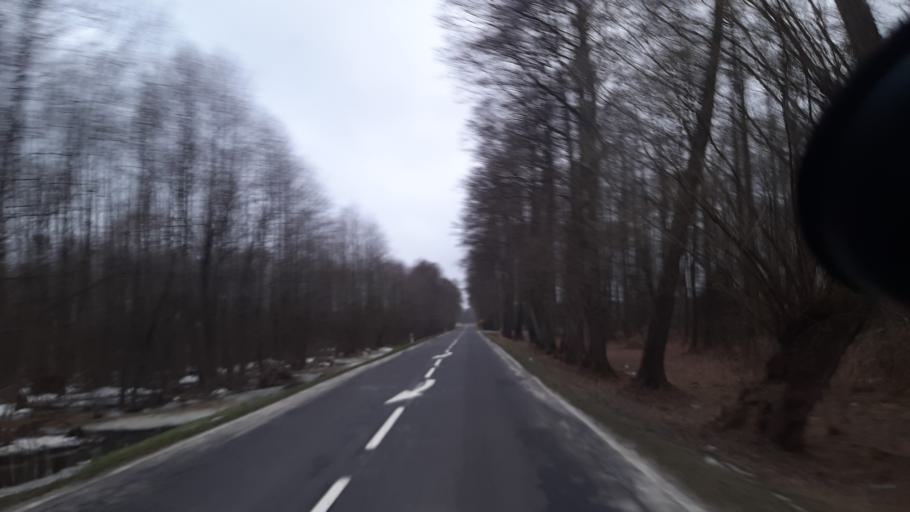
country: PL
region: Lublin Voivodeship
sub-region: Powiat parczewski
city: Podedworze
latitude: 51.5584
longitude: 23.2968
